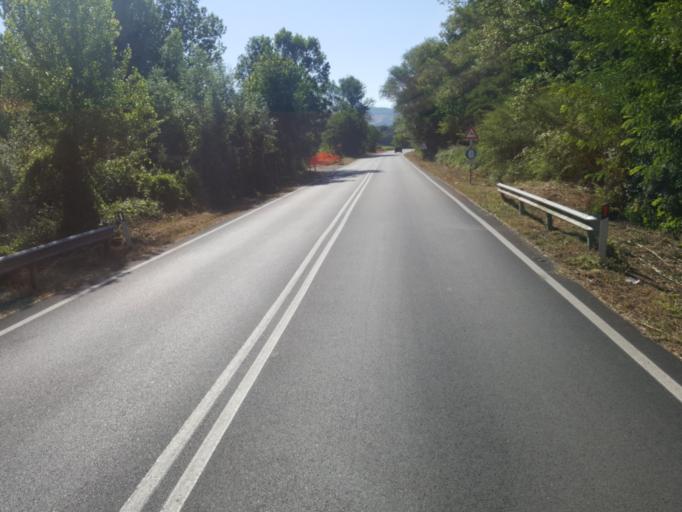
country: IT
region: The Marches
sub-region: Provincia di Pesaro e Urbino
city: Montecalvo in Foglia
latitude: 43.7947
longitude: 12.6215
